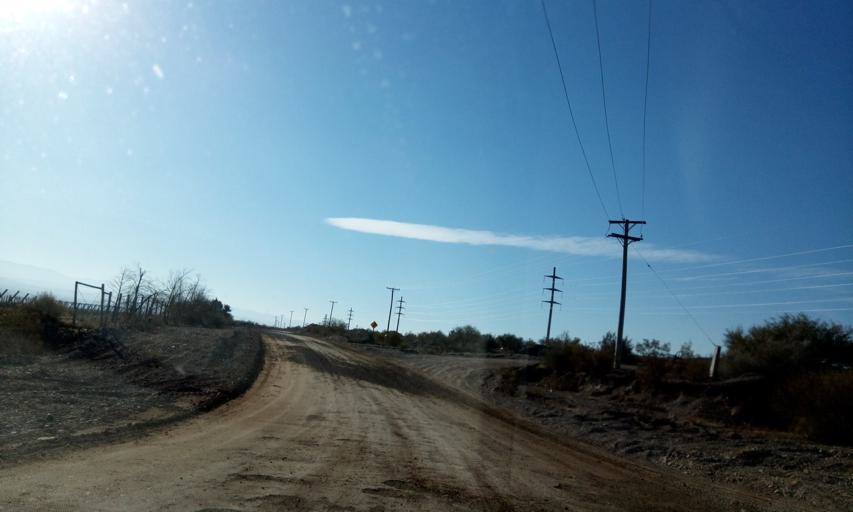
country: AR
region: San Juan
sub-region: Departamento de Rivadavia
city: Rivadavia
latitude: -31.4232
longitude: -68.6680
